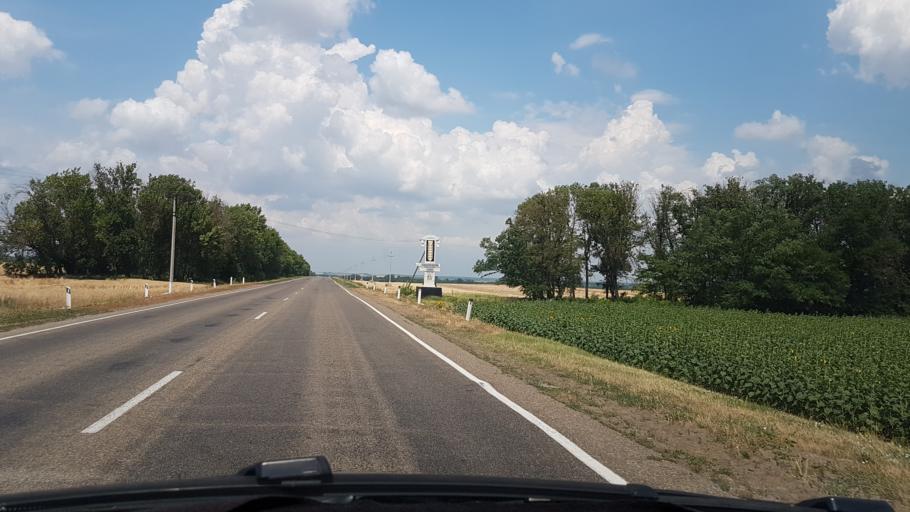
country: RU
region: Krasnodarskiy
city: Dmitriyevskaya
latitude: 45.6903
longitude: 40.7442
